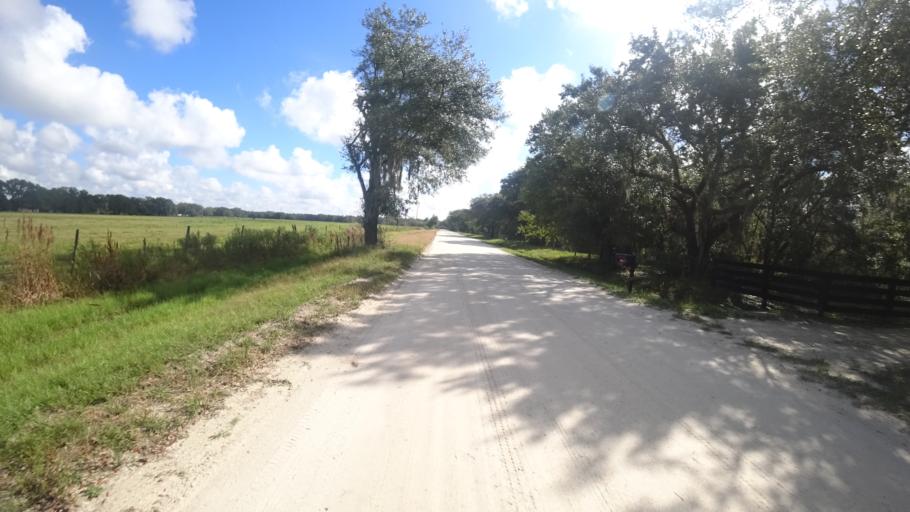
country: US
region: Florida
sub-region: Sarasota County
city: Lake Sarasota
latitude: 27.3249
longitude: -82.2182
